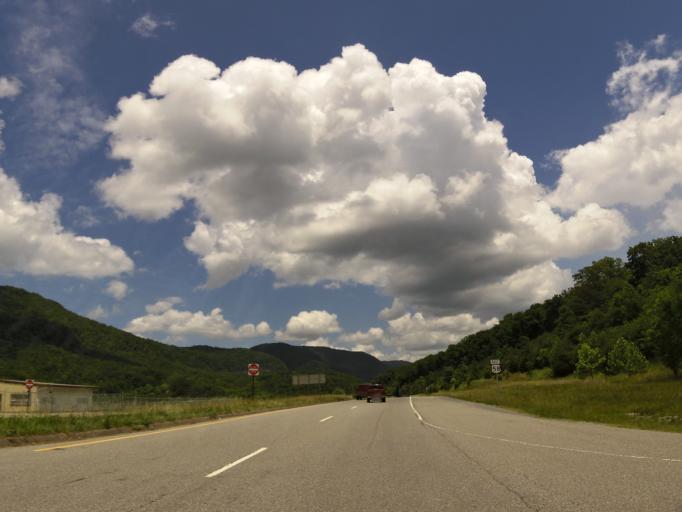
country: US
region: Tennessee
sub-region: Claiborne County
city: Harrogate
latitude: 36.5954
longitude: -83.6613
